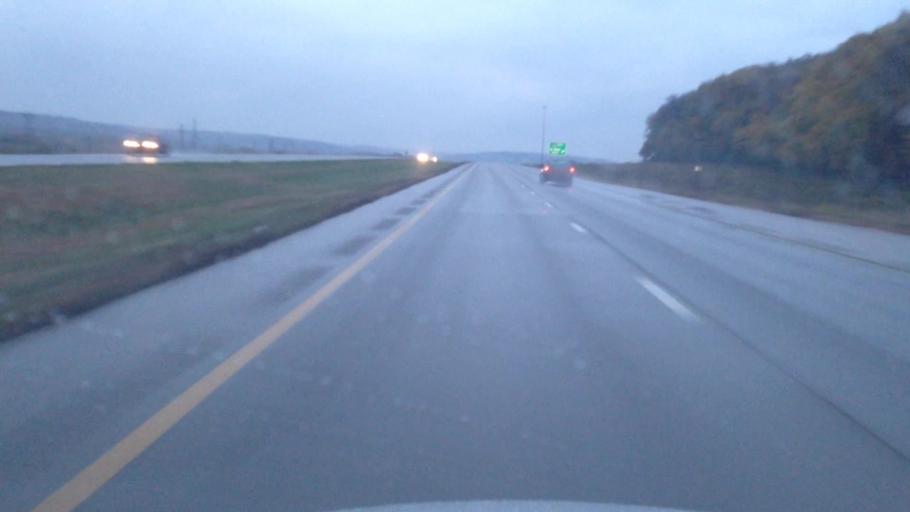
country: US
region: Kansas
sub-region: Douglas County
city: Lawrence
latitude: 38.8909
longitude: -95.2602
